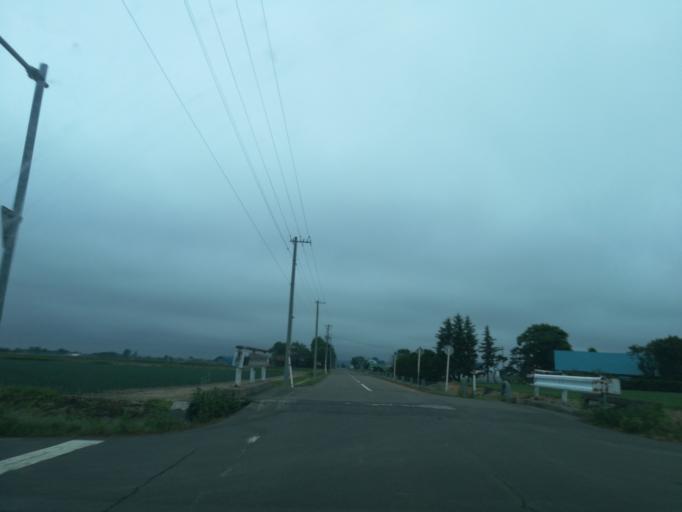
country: JP
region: Hokkaido
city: Iwamizawa
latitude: 43.1340
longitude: 141.7065
